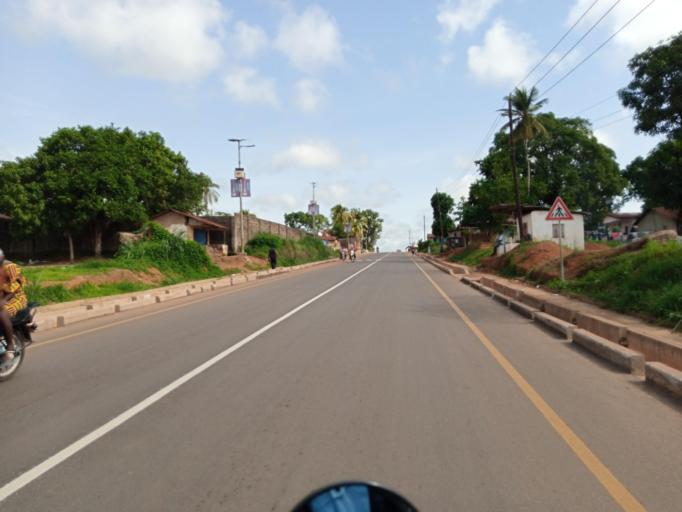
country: SL
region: Southern Province
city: Bo
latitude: 7.9526
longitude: -11.7183
